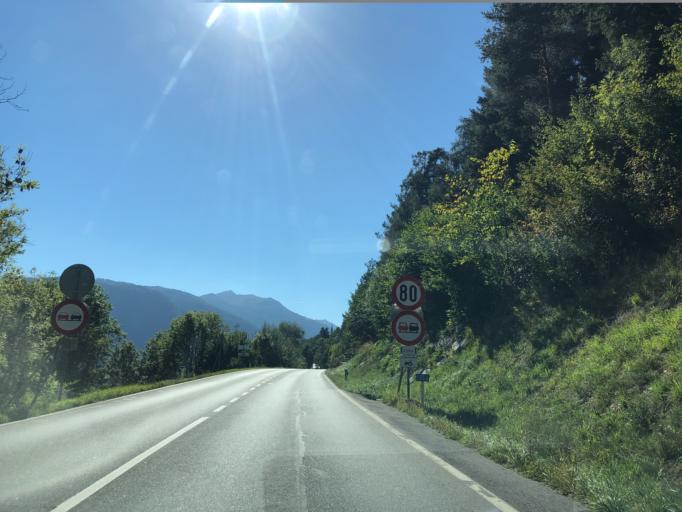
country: AT
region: Tyrol
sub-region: Politischer Bezirk Imst
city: Imst
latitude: 47.2534
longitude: 10.7489
